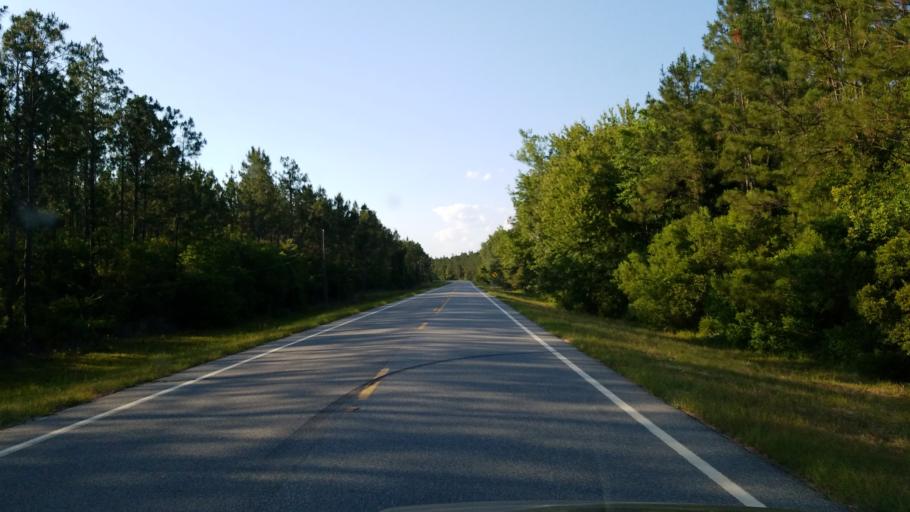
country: US
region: Georgia
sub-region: Lanier County
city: Lakeland
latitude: 30.8820
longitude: -83.0531
